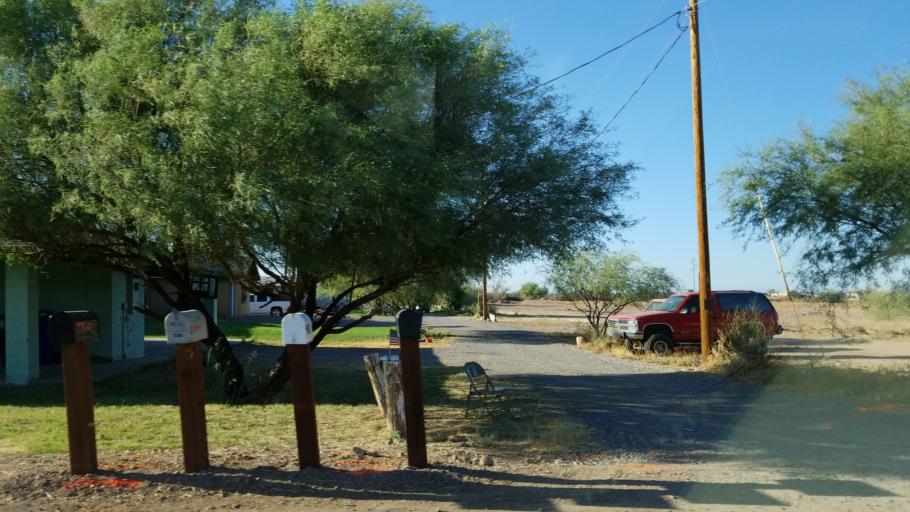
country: US
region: Arizona
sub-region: Maricopa County
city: Laveen
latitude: 33.3774
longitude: -112.2327
